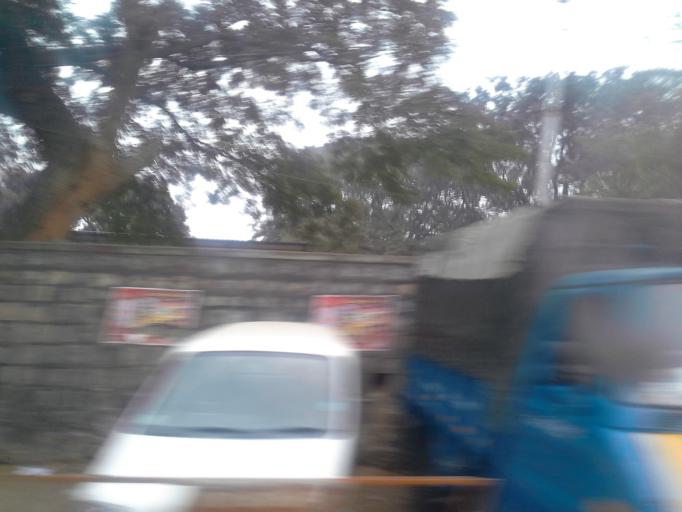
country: IN
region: Karnataka
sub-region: Bangalore Urban
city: Bangalore
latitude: 12.9803
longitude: 77.6119
